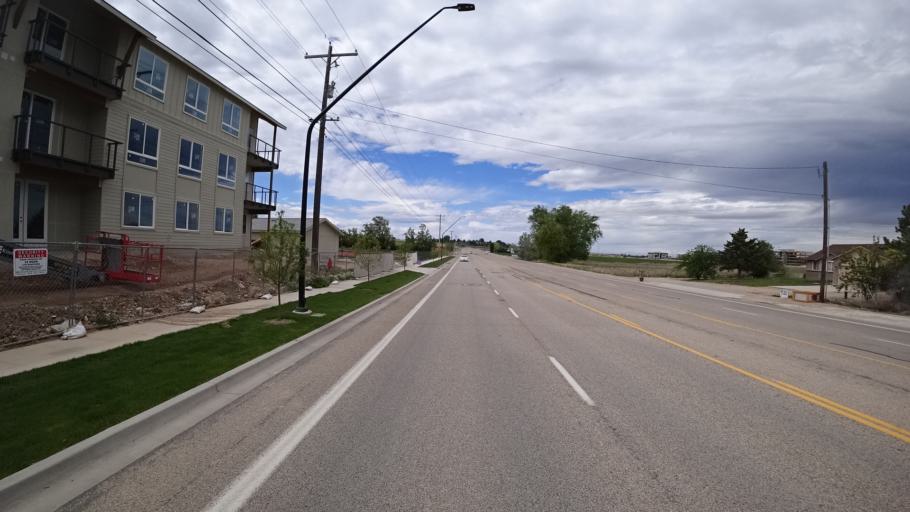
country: US
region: Idaho
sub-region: Ada County
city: Meridian
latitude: 43.5901
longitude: -116.4185
